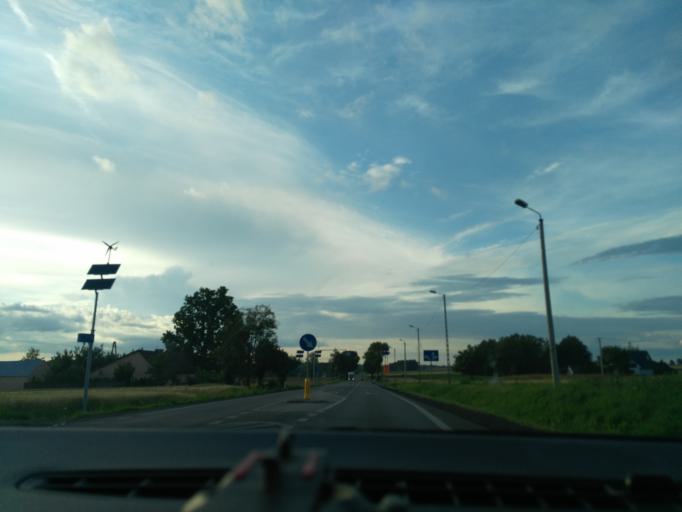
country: PL
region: Lublin Voivodeship
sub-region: Powiat lubelski
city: Niedrzwica Duza
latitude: 51.0763
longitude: 22.3750
